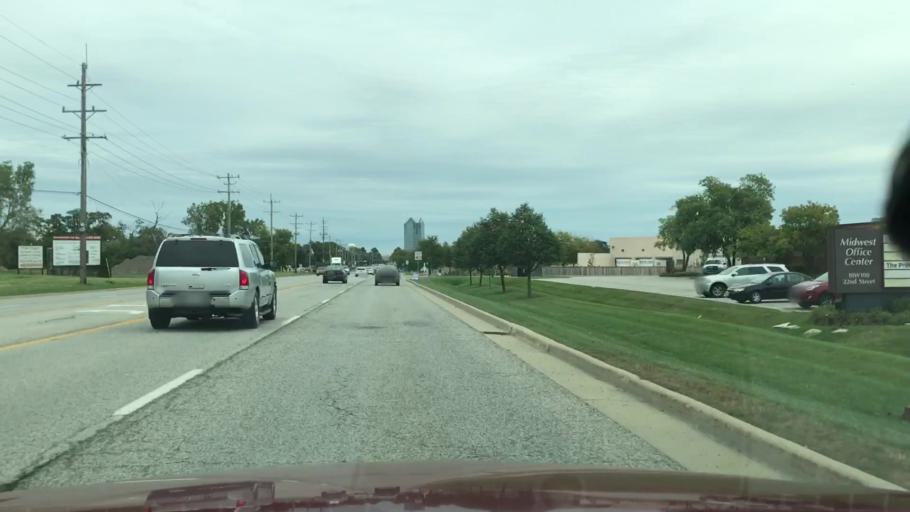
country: US
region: Illinois
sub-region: DuPage County
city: Oakbrook Terrace
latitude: 41.8479
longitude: -87.9796
